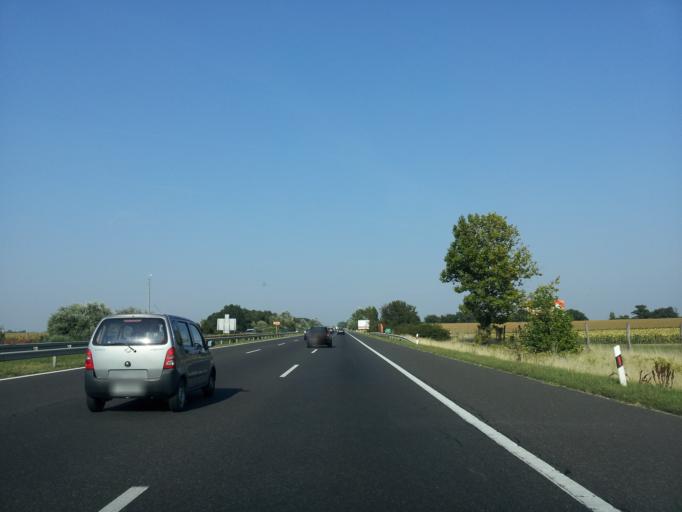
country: HU
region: Fejer
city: Kapolnasnyek
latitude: 47.2662
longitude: 18.6882
